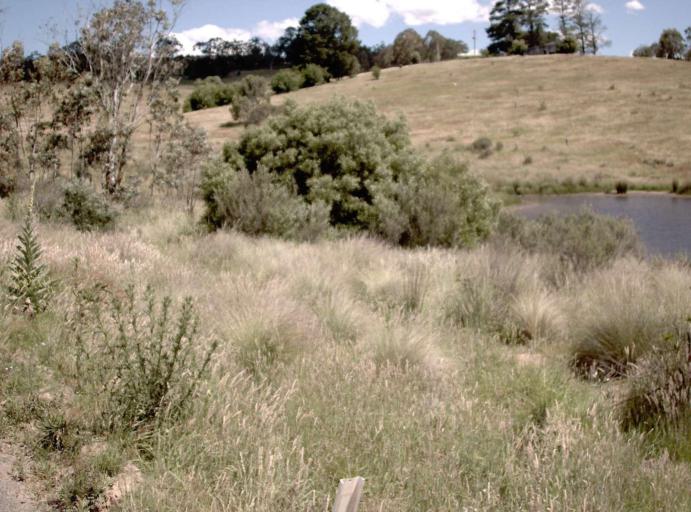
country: AU
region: New South Wales
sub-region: Bombala
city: Bombala
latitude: -37.1393
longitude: 148.6627
